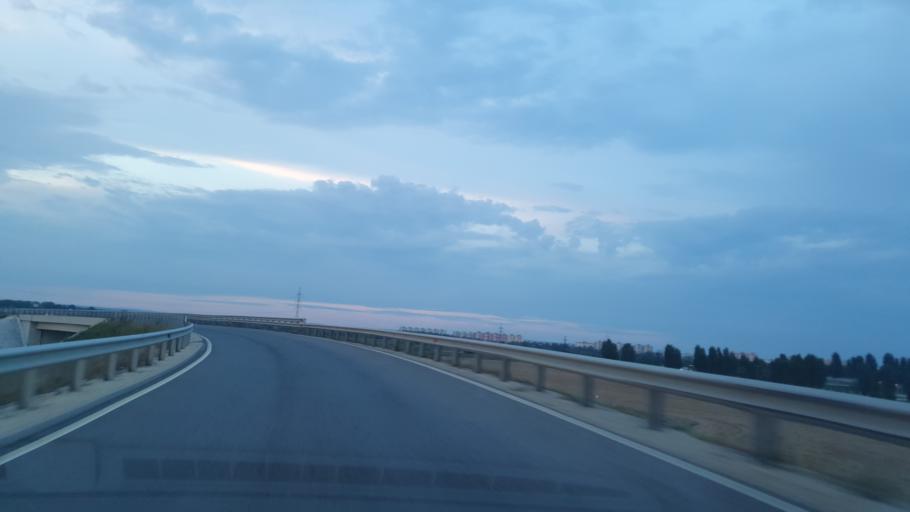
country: HU
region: Fejer
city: Szekesfehervar
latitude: 47.1816
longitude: 18.3820
